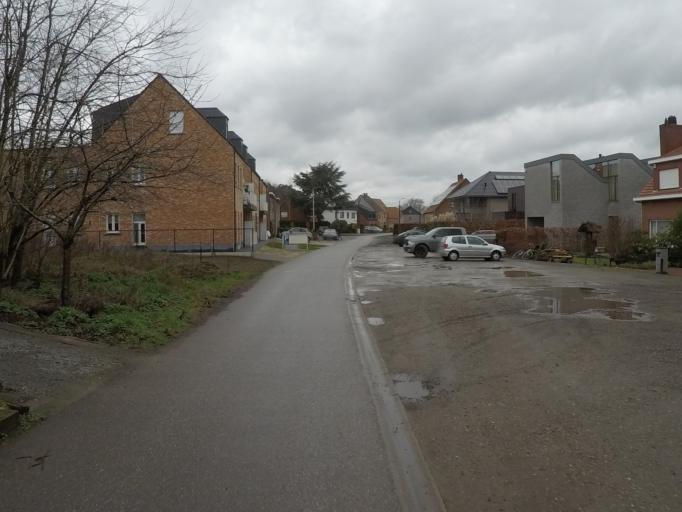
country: BE
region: Flanders
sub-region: Provincie Antwerpen
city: Schilde
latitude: 51.2152
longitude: 4.5947
